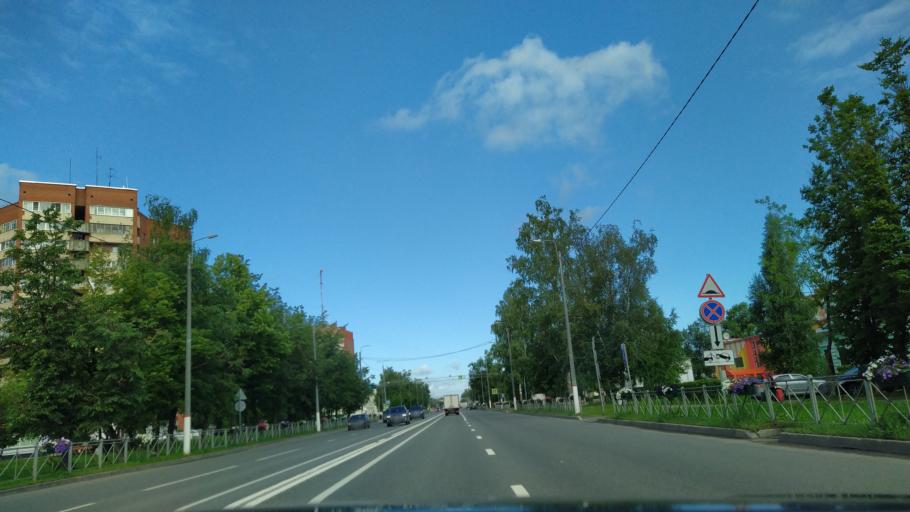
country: RU
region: Leningrad
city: Tosno
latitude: 59.5383
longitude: 30.8819
